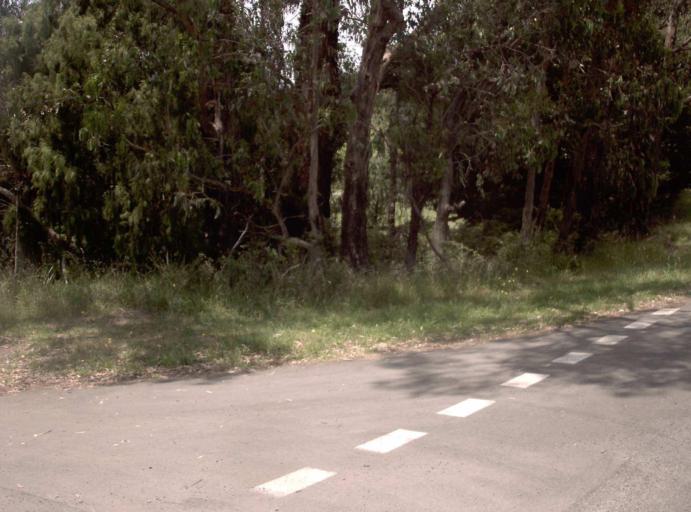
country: AU
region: Victoria
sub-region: Latrobe
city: Traralgon
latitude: -38.3774
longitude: 146.7545
